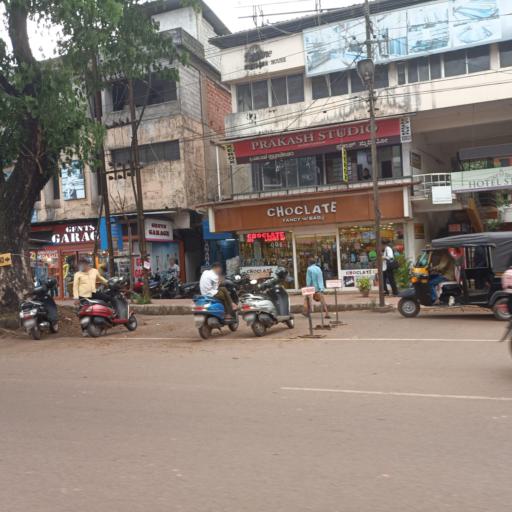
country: IN
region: Kerala
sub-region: Kasaragod District
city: Kasaragod
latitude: 12.5019
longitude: 74.9904
